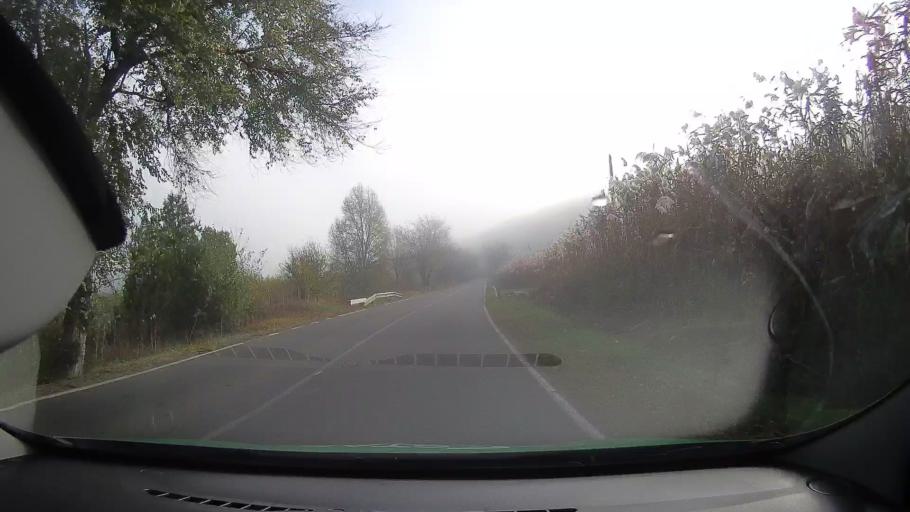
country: RO
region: Tulcea
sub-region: Comuna Nufaru
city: Nufaru
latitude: 45.1467
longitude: 28.9062
